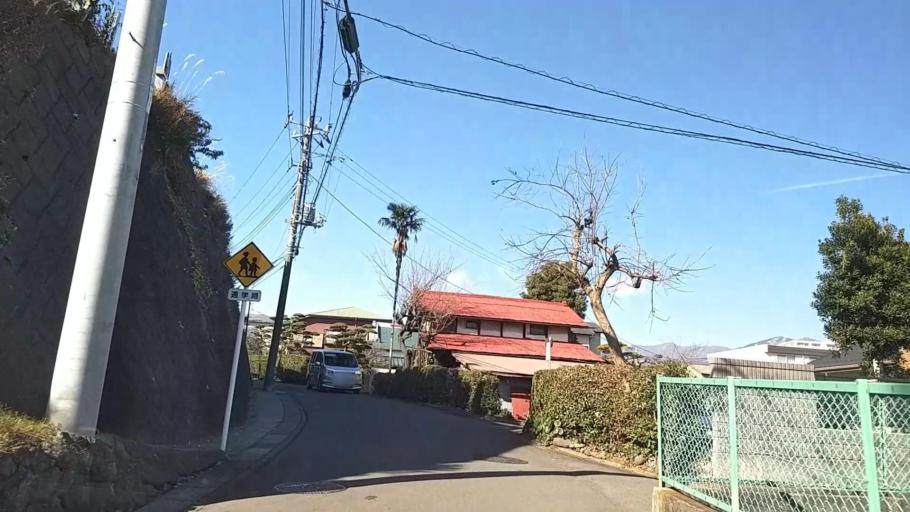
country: JP
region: Kanagawa
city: Hadano
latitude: 35.3681
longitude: 139.2296
